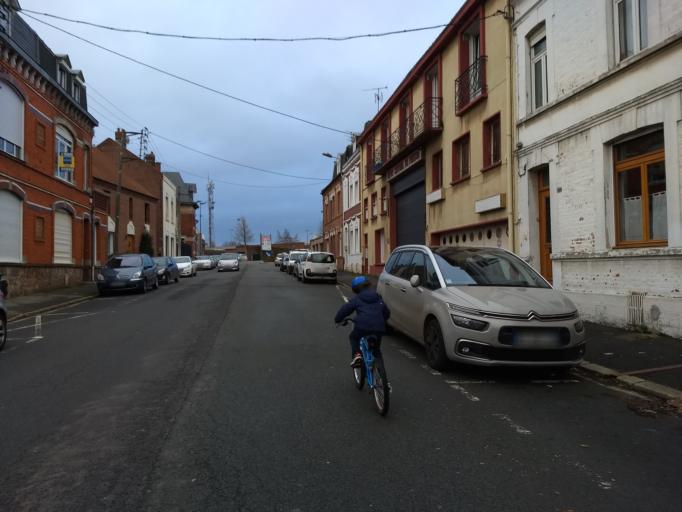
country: FR
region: Nord-Pas-de-Calais
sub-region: Departement du Pas-de-Calais
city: Arras
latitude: 50.2849
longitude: 2.7719
